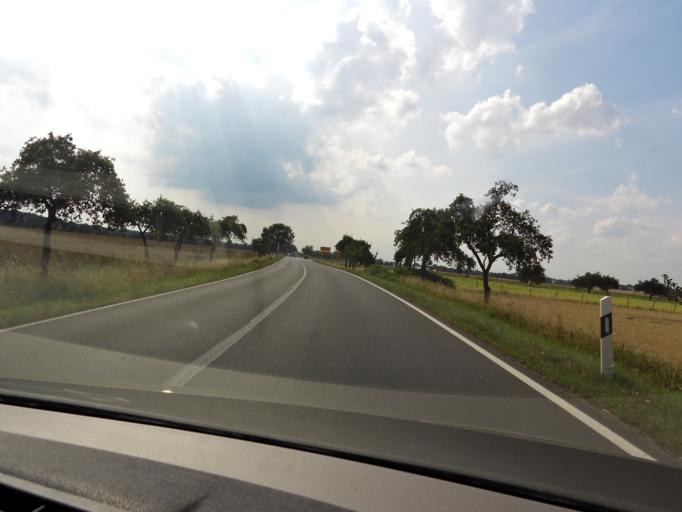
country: DE
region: Saxony
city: Grossposna
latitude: 51.2606
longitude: 12.5218
